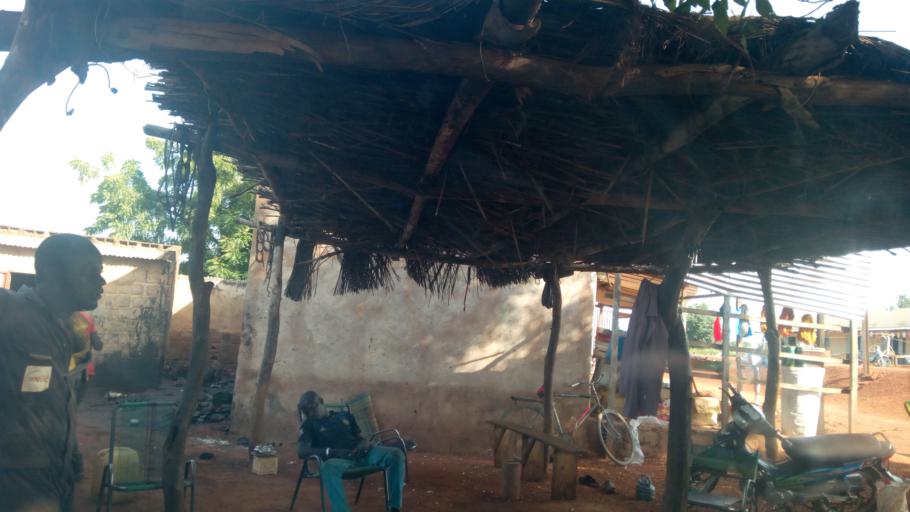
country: ML
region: Sikasso
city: Yorosso
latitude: 12.1800
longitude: -4.7996
